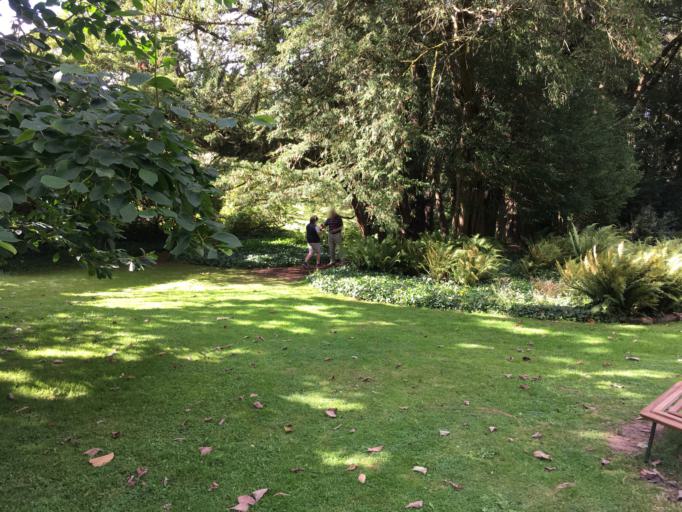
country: IE
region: Munster
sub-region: County Cork
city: Youghal
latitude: 52.1388
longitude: -7.9319
